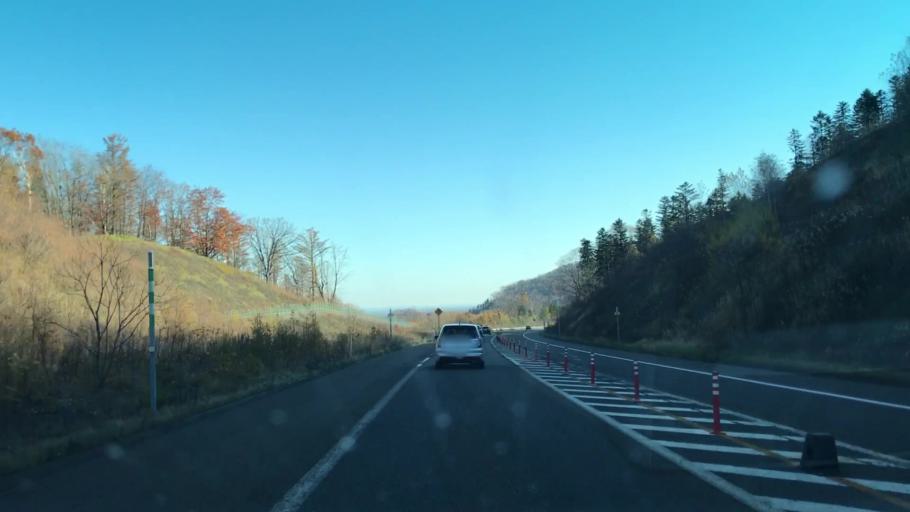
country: JP
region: Hokkaido
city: Otofuke
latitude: 43.0166
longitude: 142.8286
